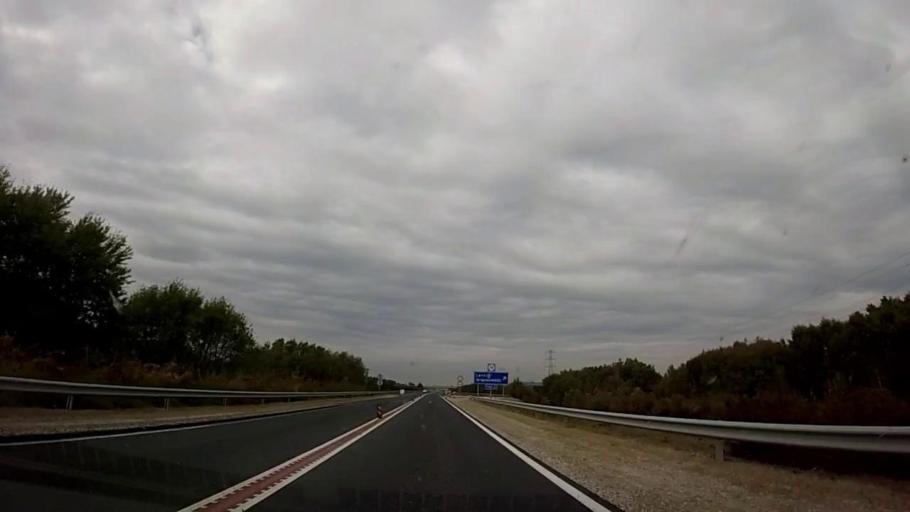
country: HR
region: Medimurska
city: Podturen
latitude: 46.5065
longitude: 16.5841
